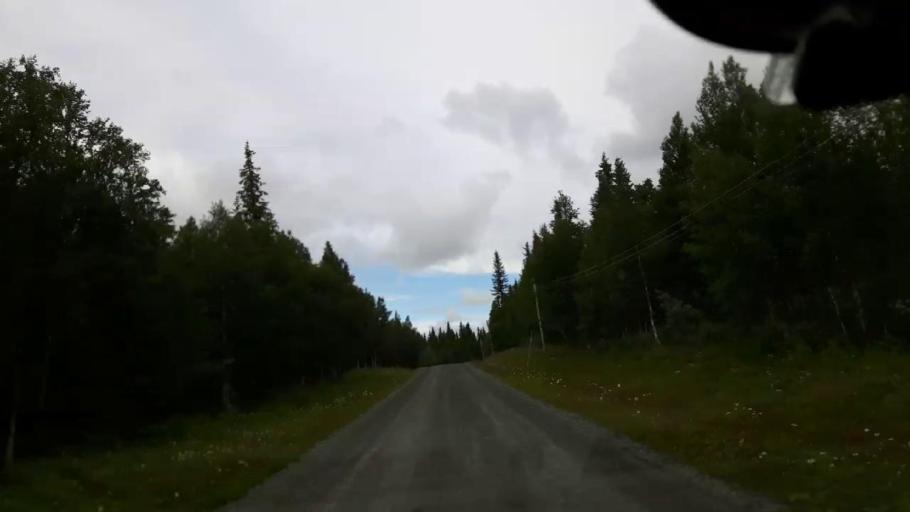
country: SE
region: Jaemtland
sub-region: Krokoms Kommun
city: Valla
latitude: 63.7686
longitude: 13.8322
